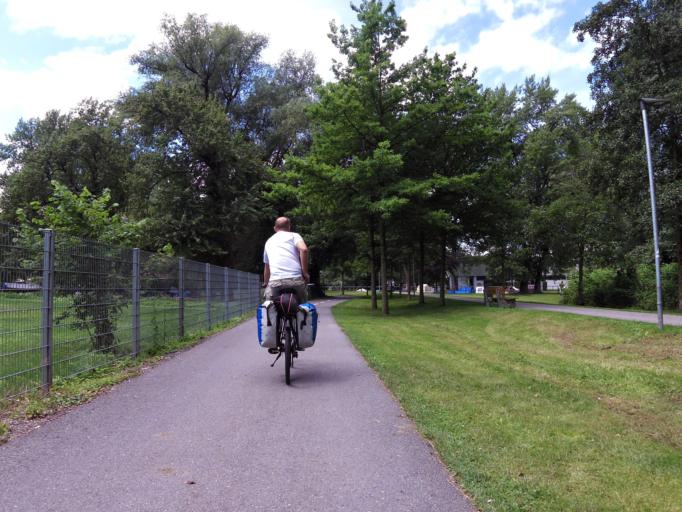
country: AT
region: Vorarlberg
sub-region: Politischer Bezirk Bregenz
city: Bregenz
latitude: 47.5057
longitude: 9.7304
